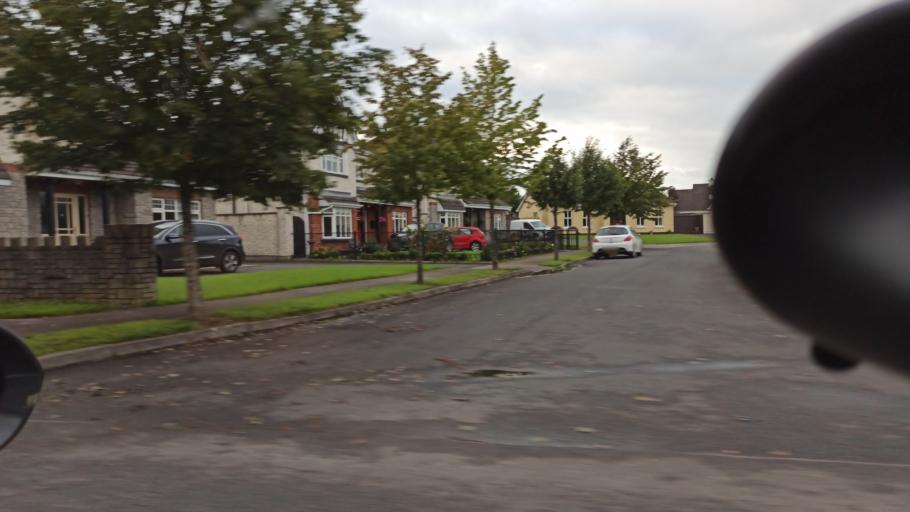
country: IE
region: Munster
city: Thurles
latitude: 52.6674
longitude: -7.8122
